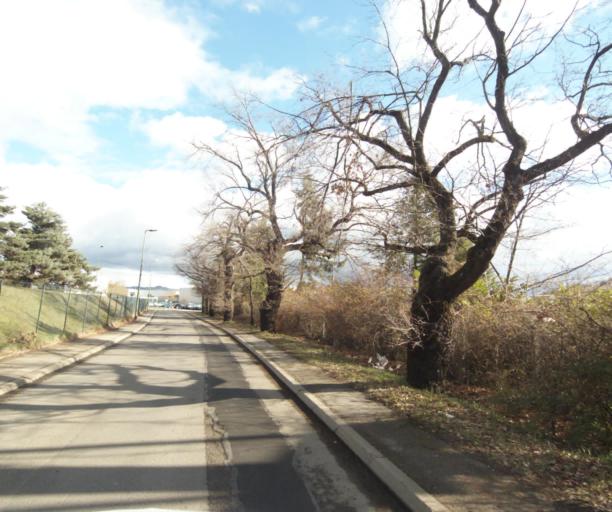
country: FR
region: Rhone-Alpes
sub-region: Departement de la Loire
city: La Talaudiere
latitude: 45.4654
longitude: 4.4238
